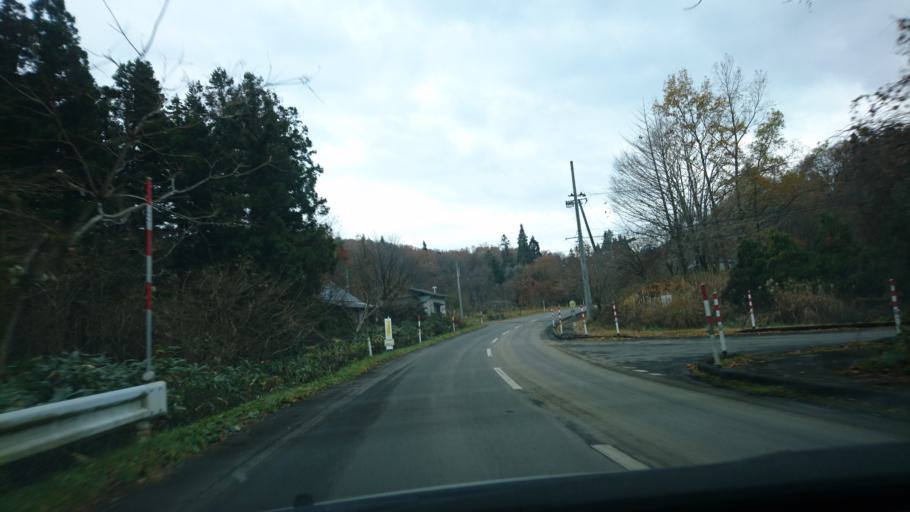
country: JP
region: Iwate
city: Ichinoseki
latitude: 38.9726
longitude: 140.9416
